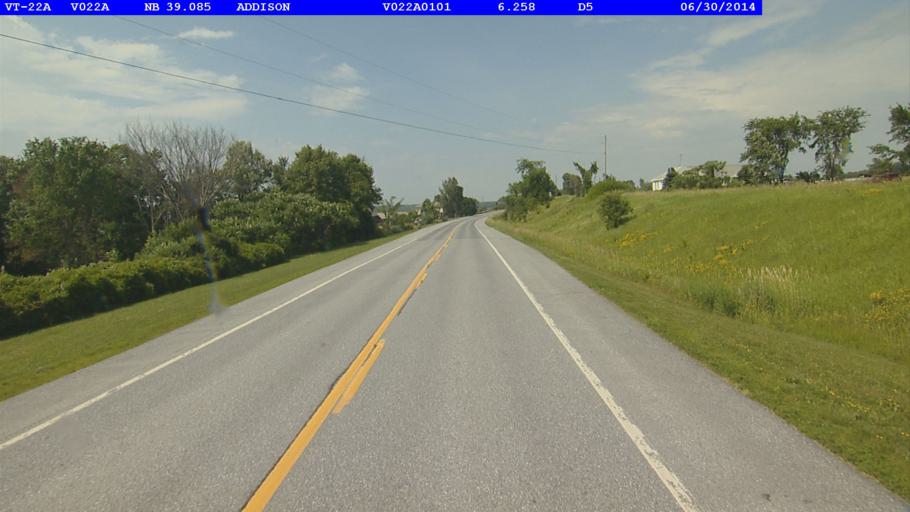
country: US
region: Vermont
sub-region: Addison County
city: Vergennes
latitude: 44.1189
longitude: -73.2936
